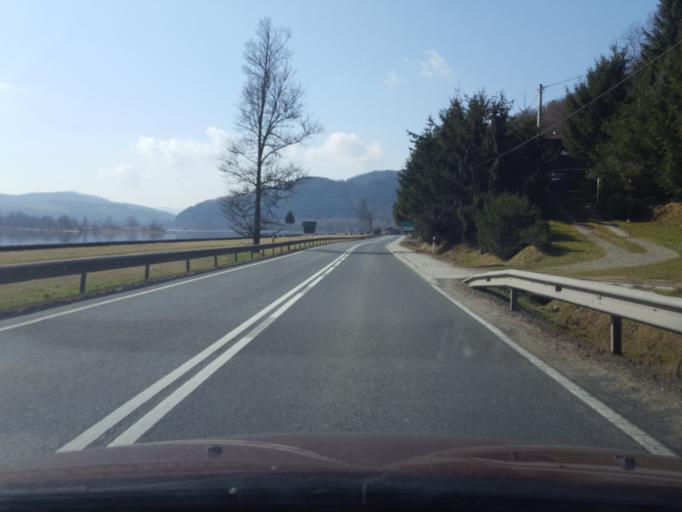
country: PL
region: Lesser Poland Voivodeship
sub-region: Powiat brzeski
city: Czchow
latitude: 49.8063
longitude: 20.6544
